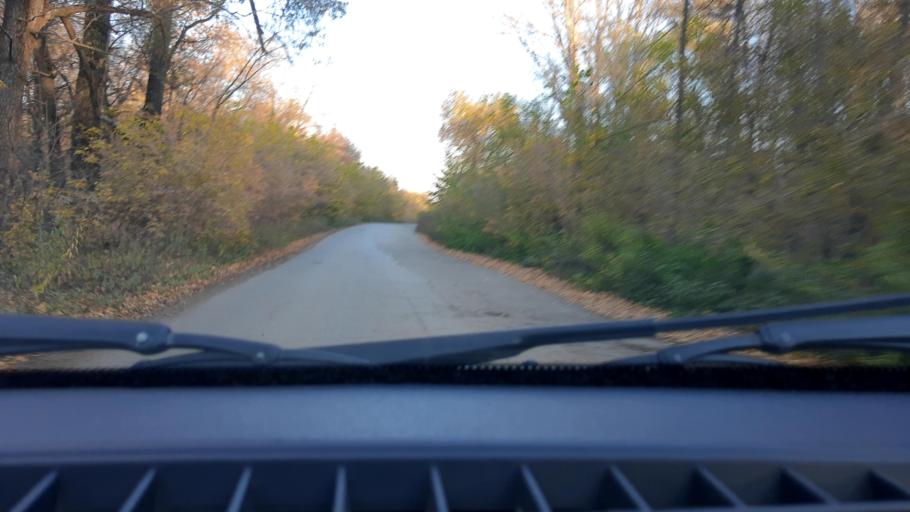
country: RU
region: Bashkortostan
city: Ufa
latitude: 54.7989
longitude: 56.1743
